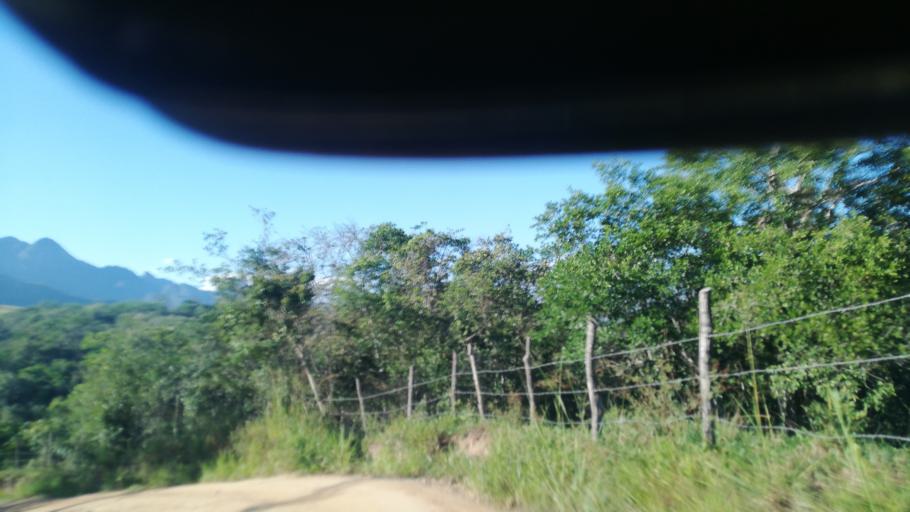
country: CO
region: Cundinamarca
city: Viani
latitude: 4.8330
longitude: -74.6199
